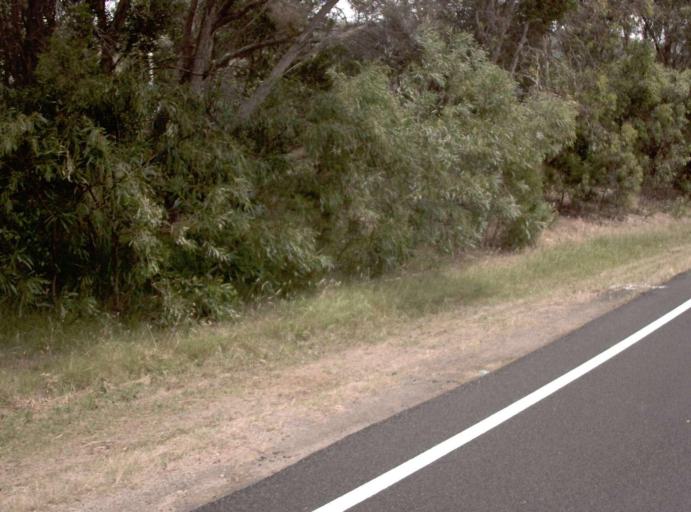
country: AU
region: Victoria
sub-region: Mornington Peninsula
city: Dromana
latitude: -38.3404
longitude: 144.9640
